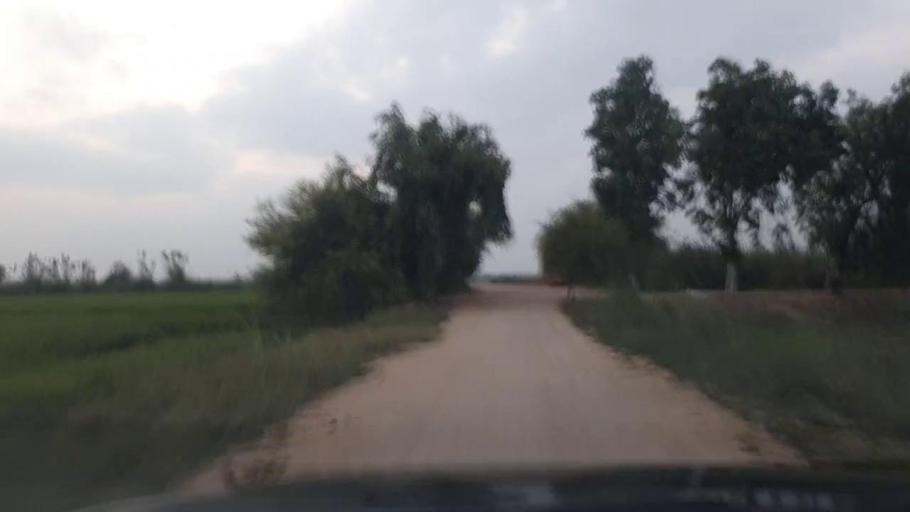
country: PK
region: Sindh
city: Jati
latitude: 24.5196
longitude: 68.3681
